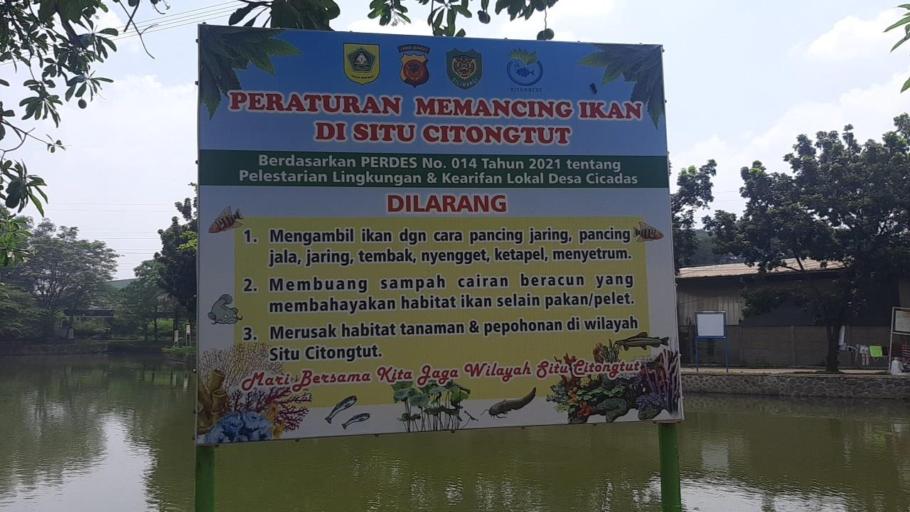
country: ID
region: West Java
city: Cileungsir
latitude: -6.4257
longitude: 106.9352
